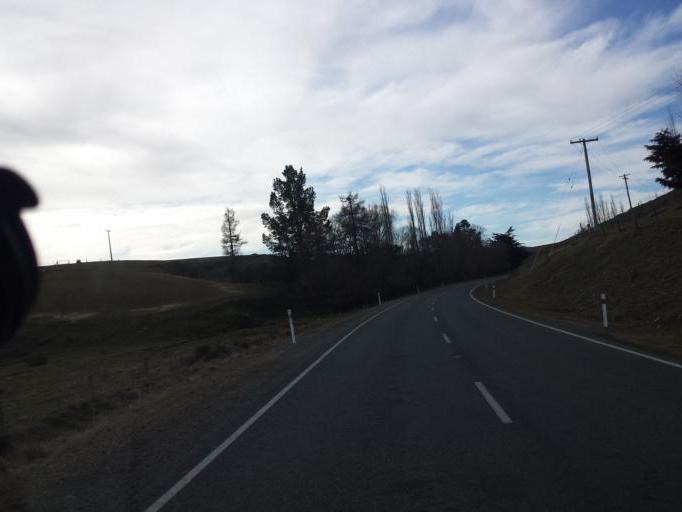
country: NZ
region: Canterbury
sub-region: Timaru District
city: Pleasant Point
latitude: -44.0670
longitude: 170.8697
